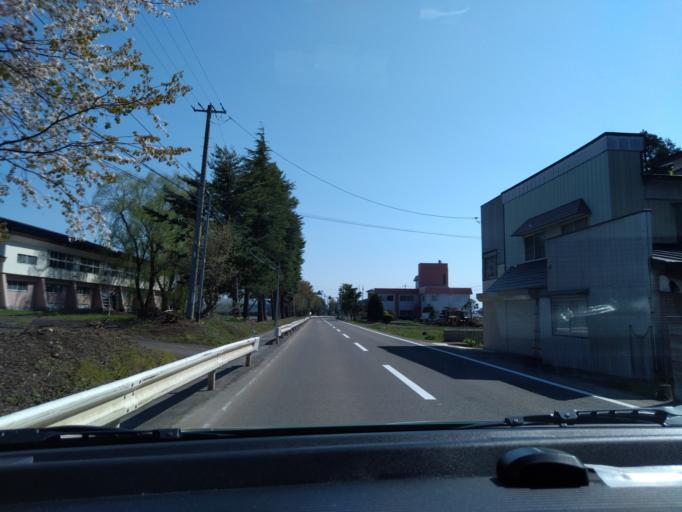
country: JP
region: Akita
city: Omagari
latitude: 39.4658
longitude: 140.5822
